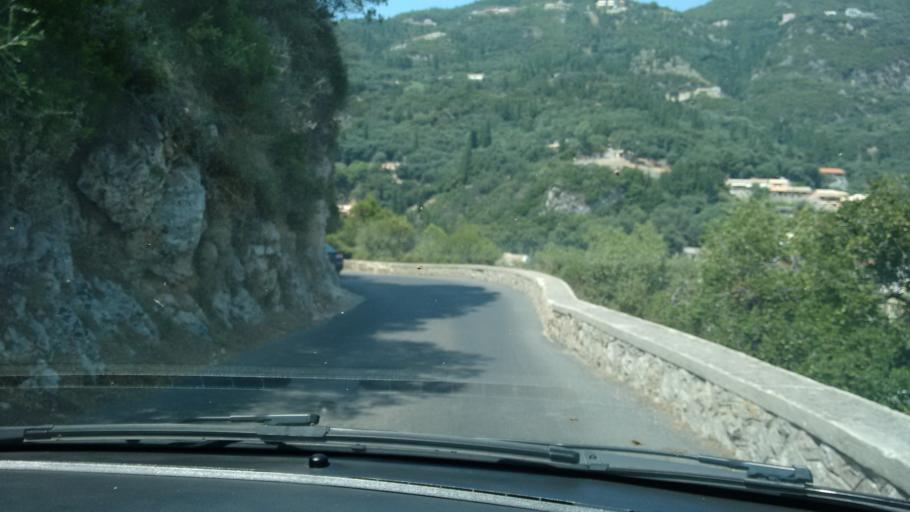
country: GR
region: Ionian Islands
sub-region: Nomos Kerkyras
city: Agios Georgis
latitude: 39.6719
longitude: 19.7020
